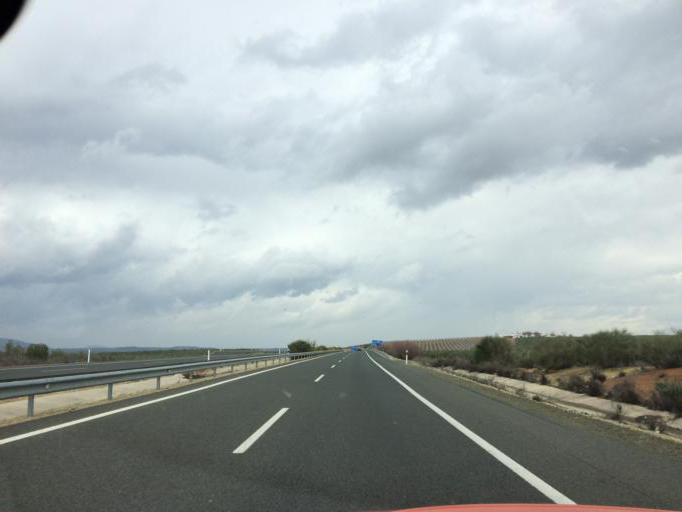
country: ES
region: Andalusia
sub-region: Provincia de Malaga
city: Antequera
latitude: 37.0955
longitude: -4.5522
